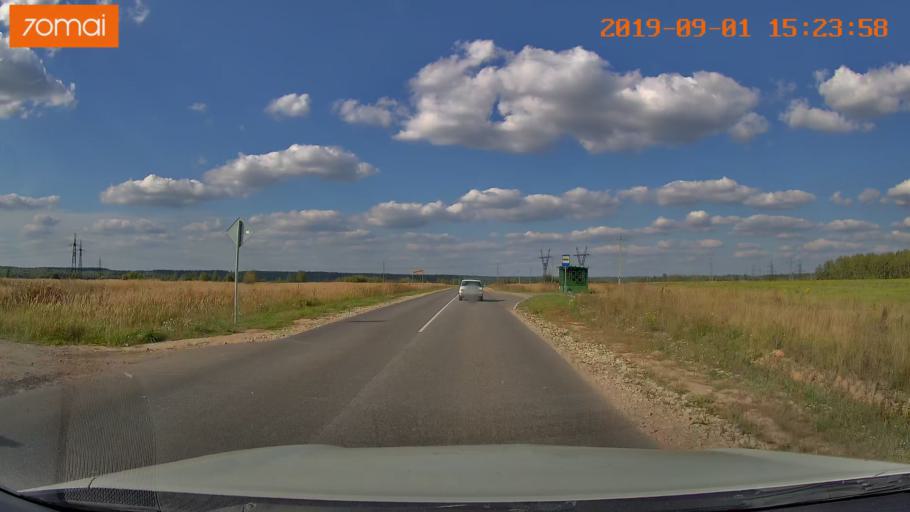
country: RU
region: Kaluga
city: Maloyaroslavets
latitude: 54.9493
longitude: 36.4585
